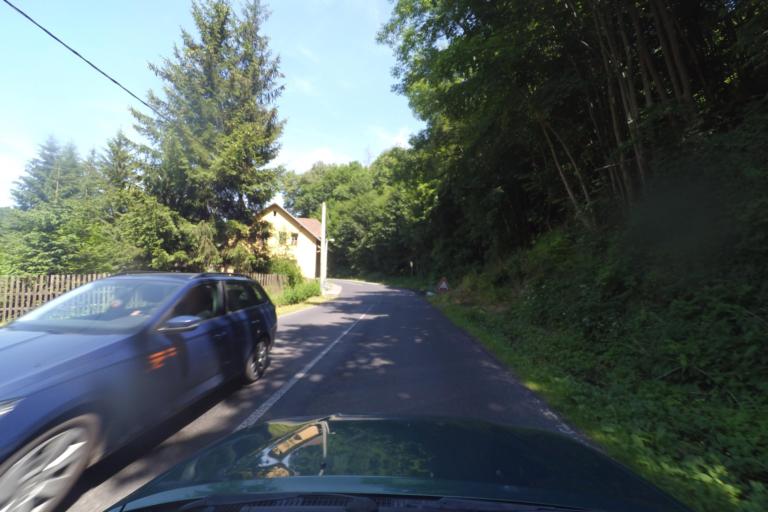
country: CZ
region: Ustecky
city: Benesov nad Ploucnici
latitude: 50.7220
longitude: 14.3237
